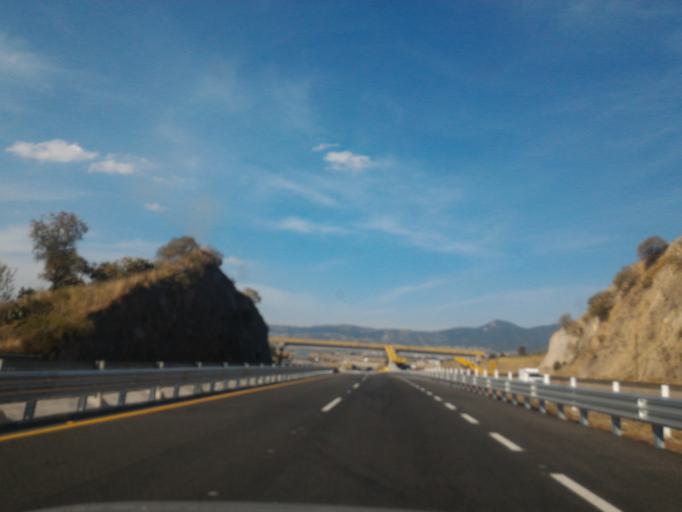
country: MX
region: Mexico
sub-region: Atlacomulco
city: San Bartolo Lanzados
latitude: 19.8973
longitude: -99.8520
